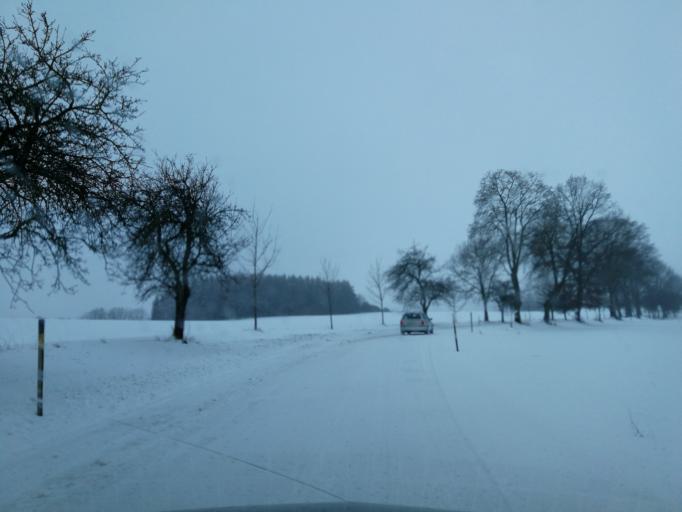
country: CZ
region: Vysocina
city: Heralec
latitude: 49.5326
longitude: 15.4343
